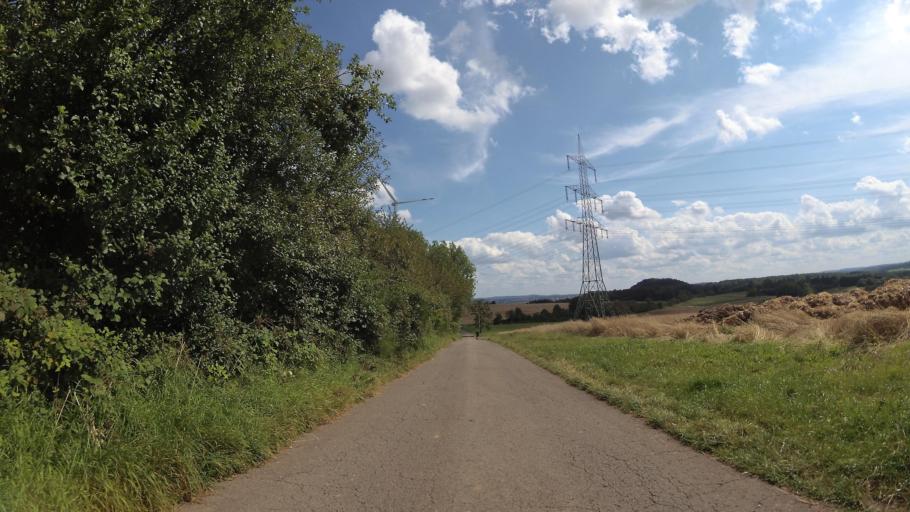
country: DE
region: Saarland
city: Schiffweiler
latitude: 49.3829
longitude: 7.1450
